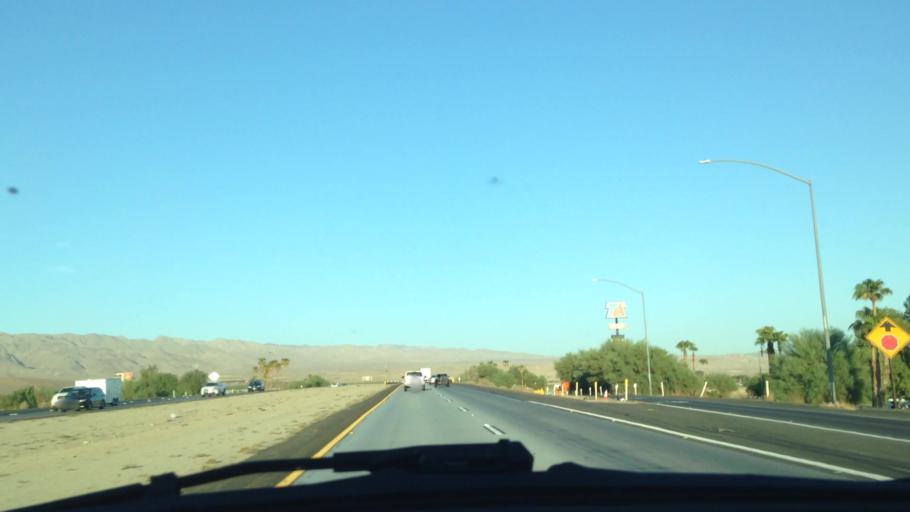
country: US
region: California
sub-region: Riverside County
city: Coachella
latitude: 33.7146
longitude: -116.1775
